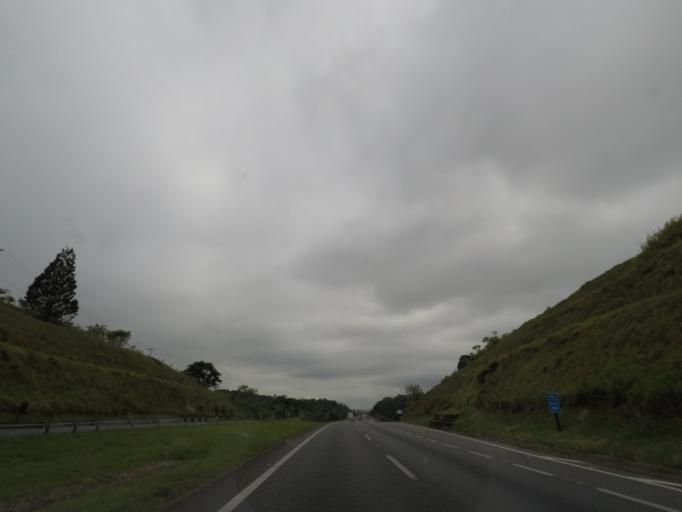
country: BR
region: Sao Paulo
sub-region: Itatiba
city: Itatiba
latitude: -22.9639
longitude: -46.8448
